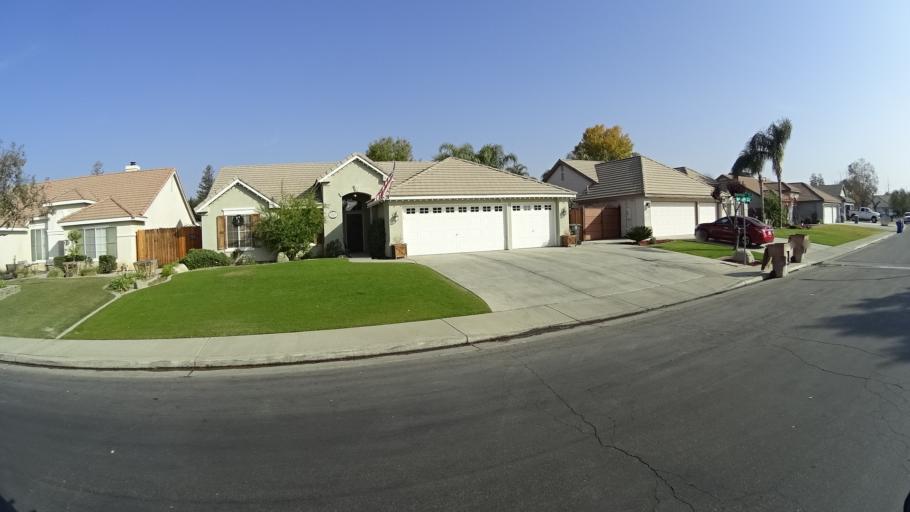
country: US
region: California
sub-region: Kern County
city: Greenacres
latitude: 35.4107
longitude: -119.1148
